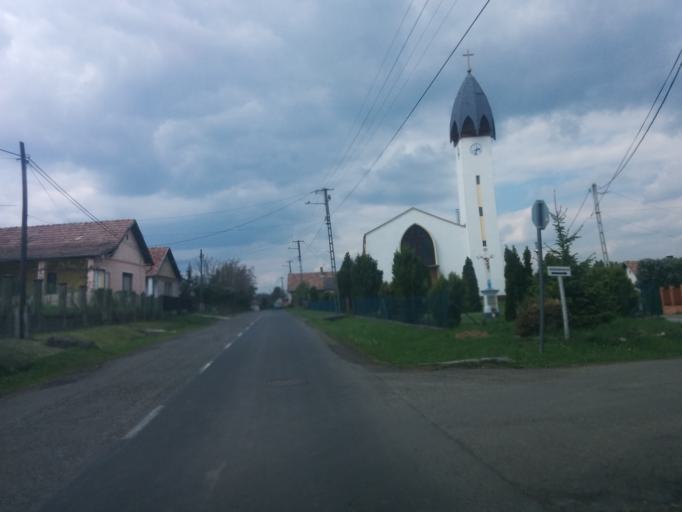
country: HU
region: Nograd
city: Palotas
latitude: 47.8232
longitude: 19.5846
